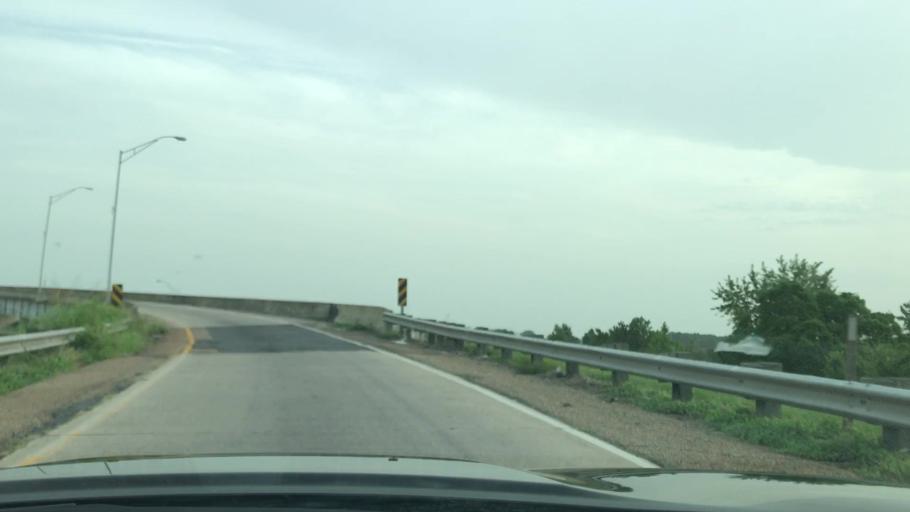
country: US
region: Louisiana
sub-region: Caddo Parish
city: Shreveport
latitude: 32.4541
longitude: -93.8430
